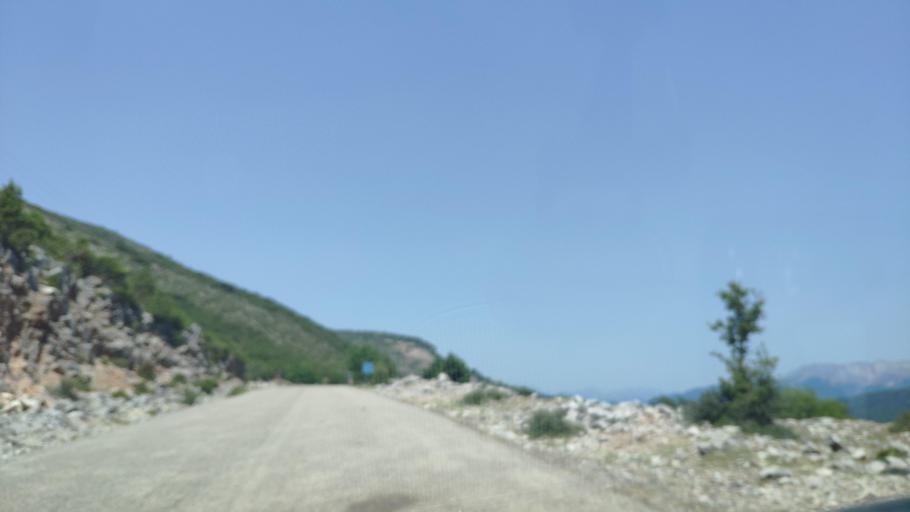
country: GR
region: Thessaly
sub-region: Nomos Kardhitsas
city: Anthiro
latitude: 39.1332
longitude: 21.3923
